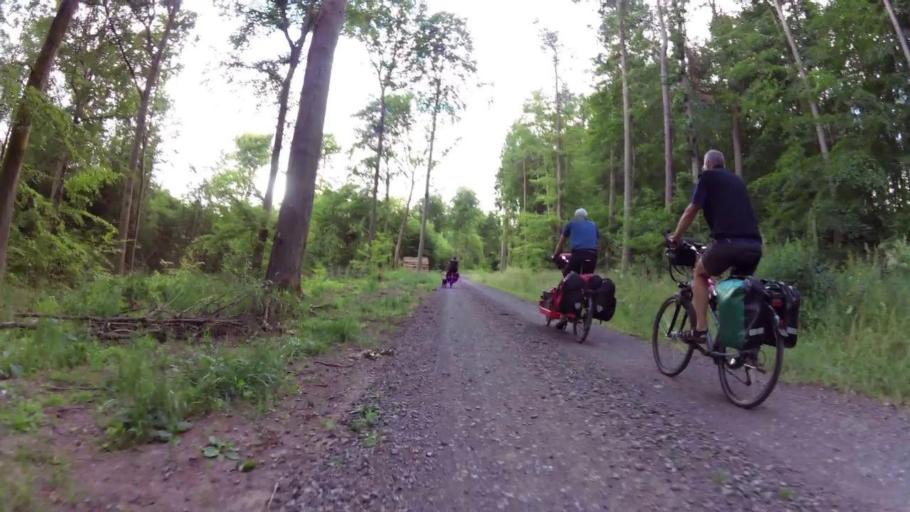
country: PL
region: West Pomeranian Voivodeship
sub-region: Powiat lobeski
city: Lobez
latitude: 53.6905
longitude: 15.5464
